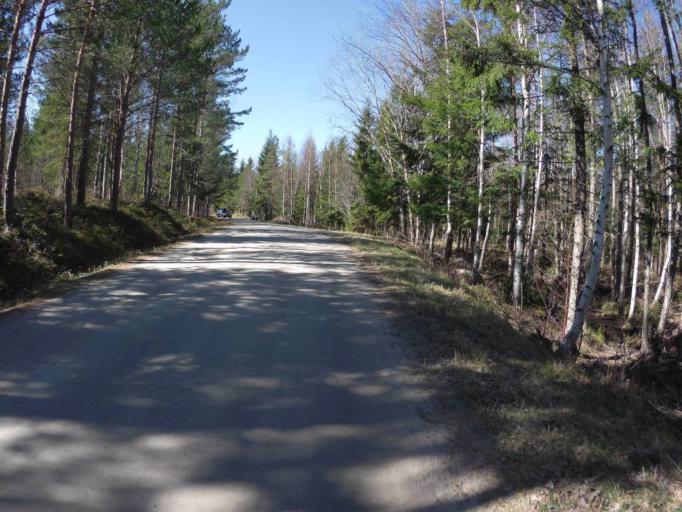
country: SE
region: Gaevleborg
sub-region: Gavle Kommun
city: Gavle
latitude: 60.7442
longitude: 17.2373
